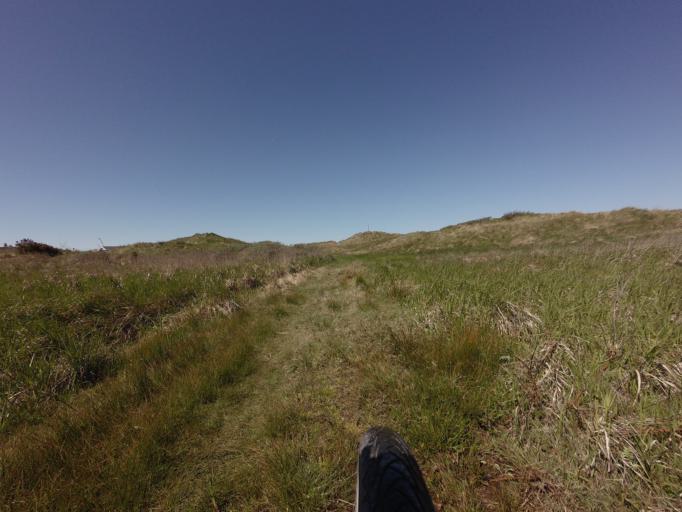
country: DK
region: North Denmark
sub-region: Jammerbugt Kommune
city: Pandrup
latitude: 57.2331
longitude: 9.5576
